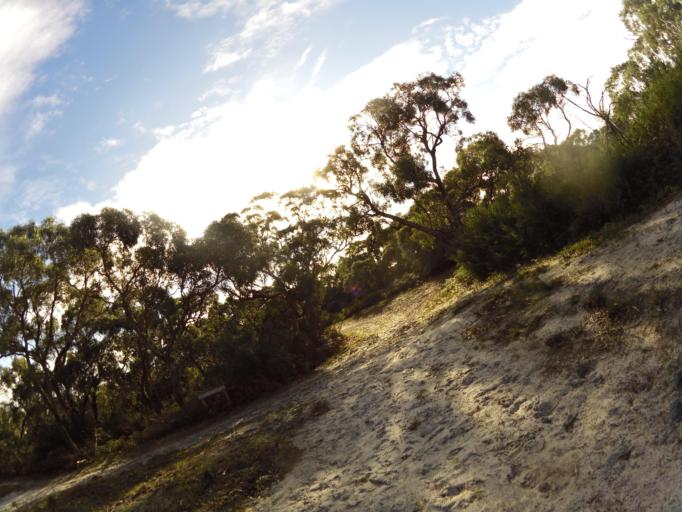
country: AU
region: Victoria
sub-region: Bass Coast
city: North Wonthaggi
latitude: -38.6320
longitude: 145.5700
